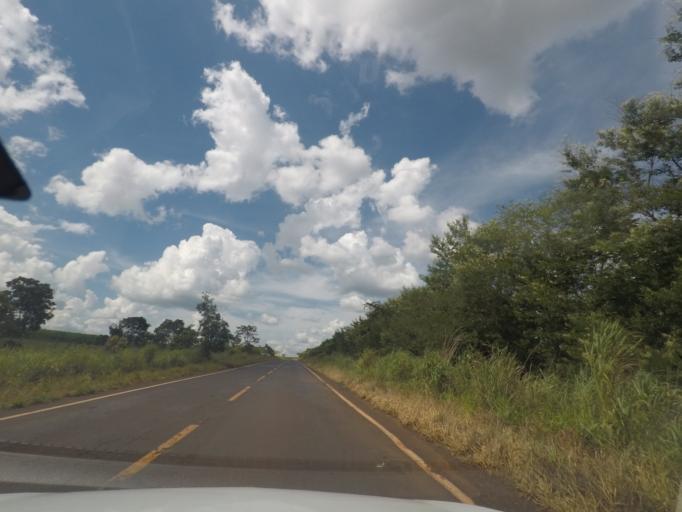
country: BR
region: Minas Gerais
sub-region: Conceicao Das Alagoas
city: Conceicao das Alagoas
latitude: -19.8146
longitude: -48.5868
